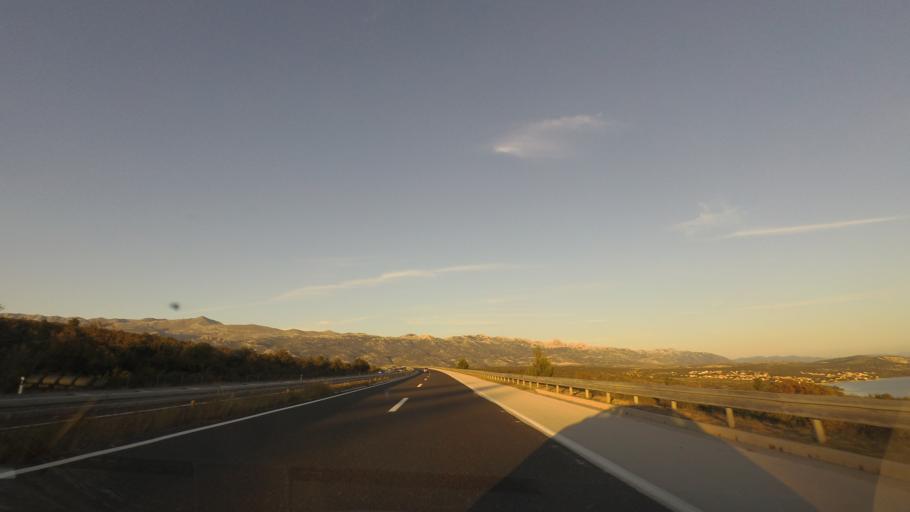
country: HR
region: Zadarska
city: Posedarje
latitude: 44.2215
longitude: 15.5028
